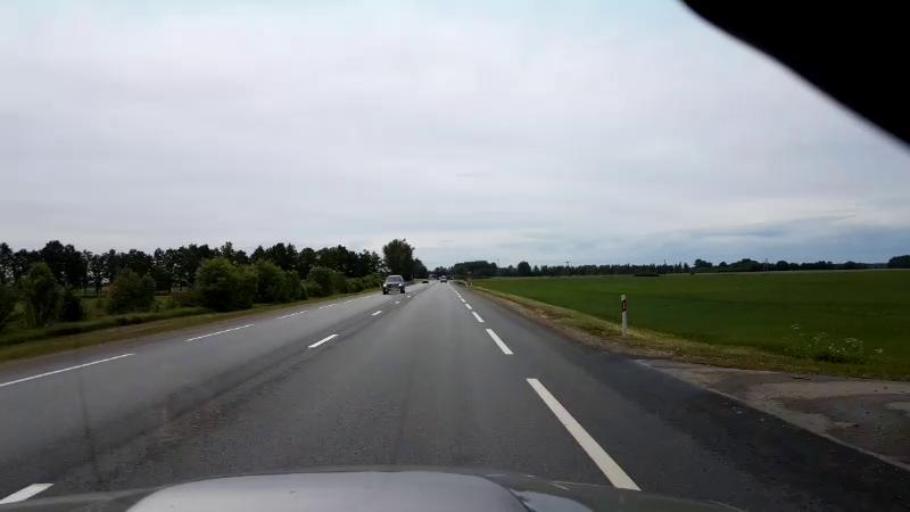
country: LV
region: Lecava
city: Iecava
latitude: 56.5824
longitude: 24.1822
